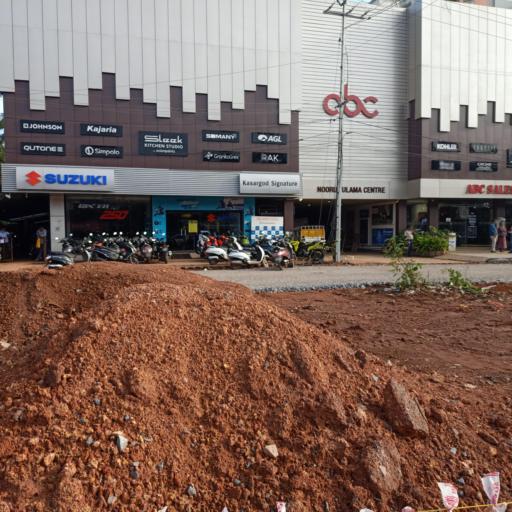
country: IN
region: Kerala
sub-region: Kasaragod District
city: Kasaragod
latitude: 12.5174
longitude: 75.0187
